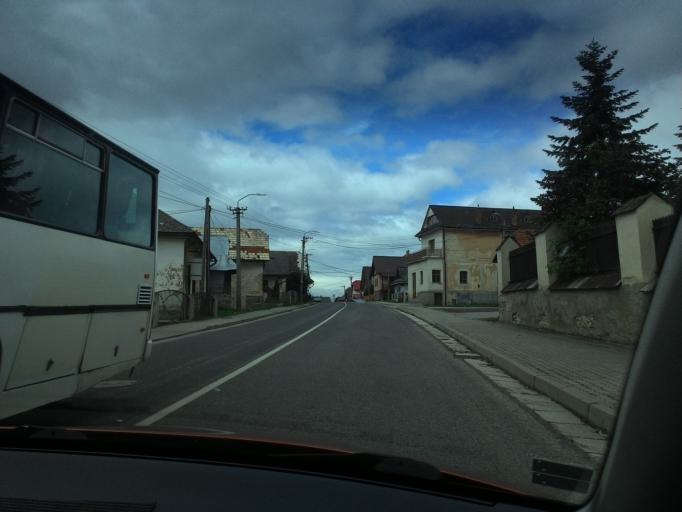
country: SK
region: Zilinsky
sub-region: Okres Liptovsky Mikulas
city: Hybe
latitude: 49.0588
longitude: 19.8885
